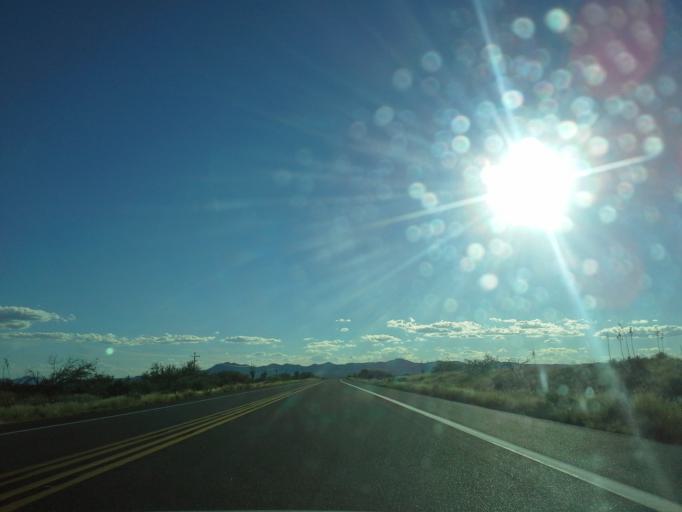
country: US
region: Arizona
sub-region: Pima County
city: Catalina
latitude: 32.5917
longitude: -110.8921
